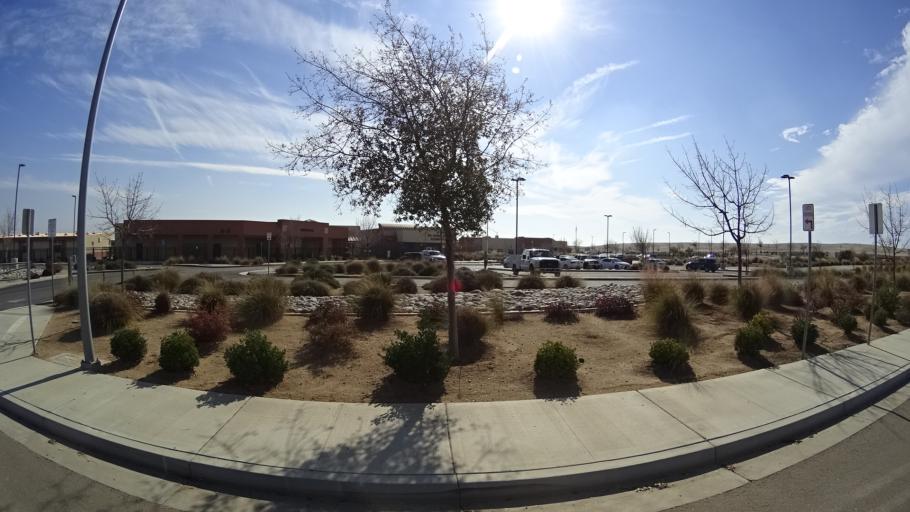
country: US
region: California
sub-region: Kern County
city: Bakersfield
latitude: 35.3924
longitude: -118.8953
